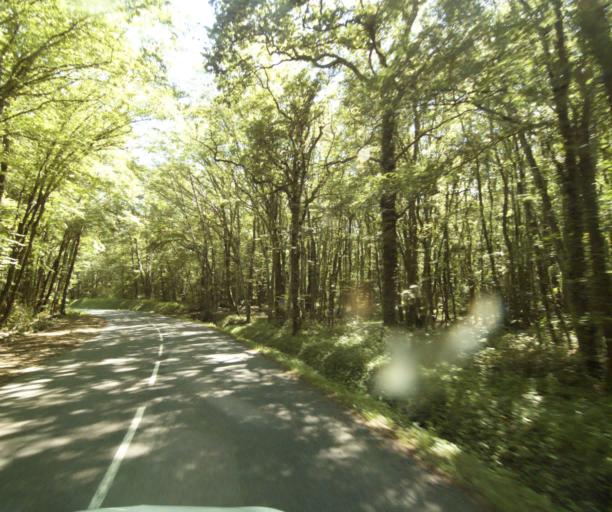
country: FR
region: Rhone-Alpes
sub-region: Departement de la Haute-Savoie
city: Ballaison
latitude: 46.2865
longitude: 6.3424
